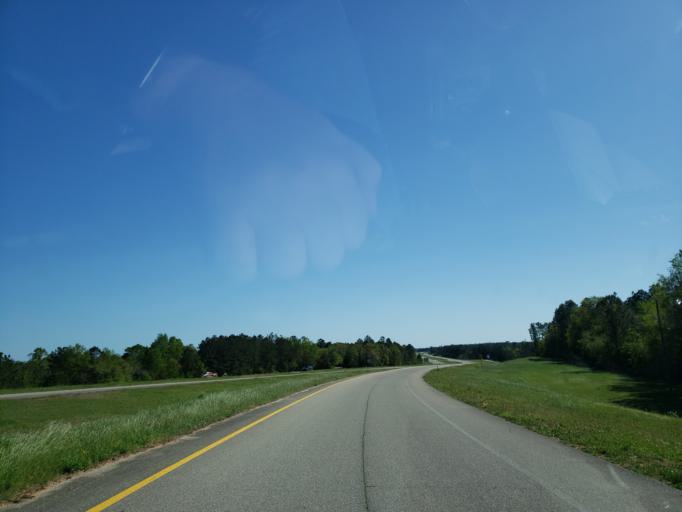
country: US
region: Mississippi
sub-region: Harrison County
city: Lyman
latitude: 30.5509
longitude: -89.0282
